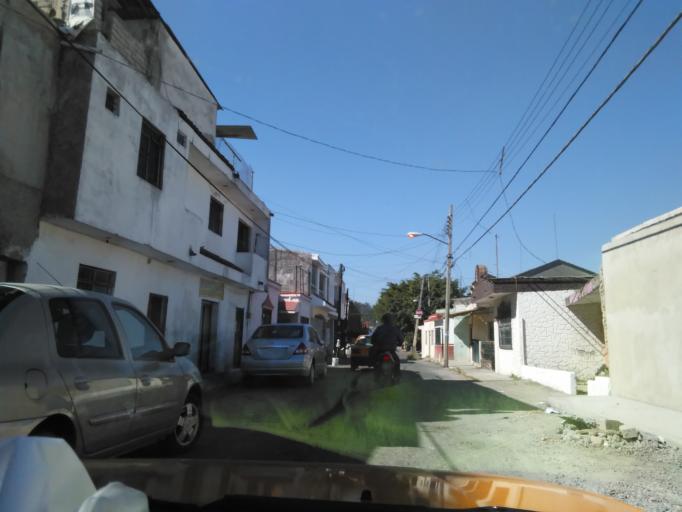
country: MX
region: Nayarit
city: Tepic
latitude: 21.5002
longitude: -104.8907
